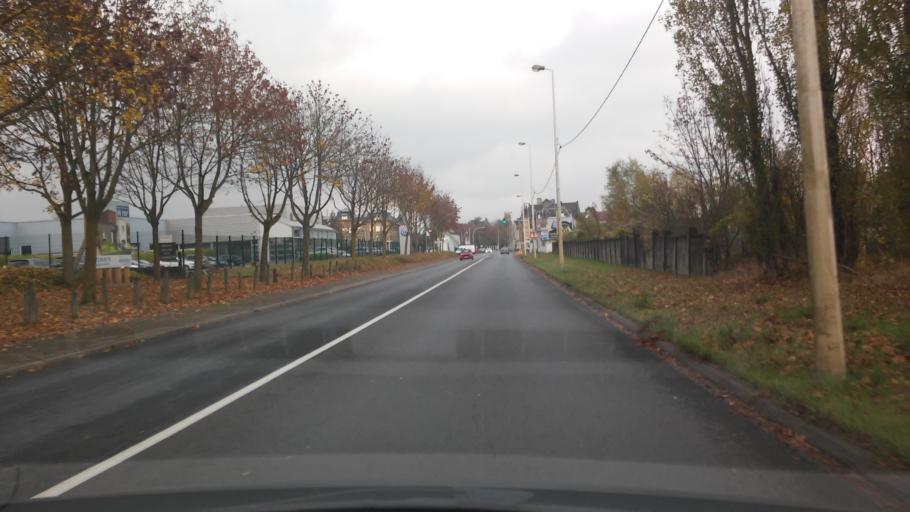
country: FR
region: Lorraine
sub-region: Departement de la Moselle
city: Terville
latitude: 49.3407
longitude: 6.1602
